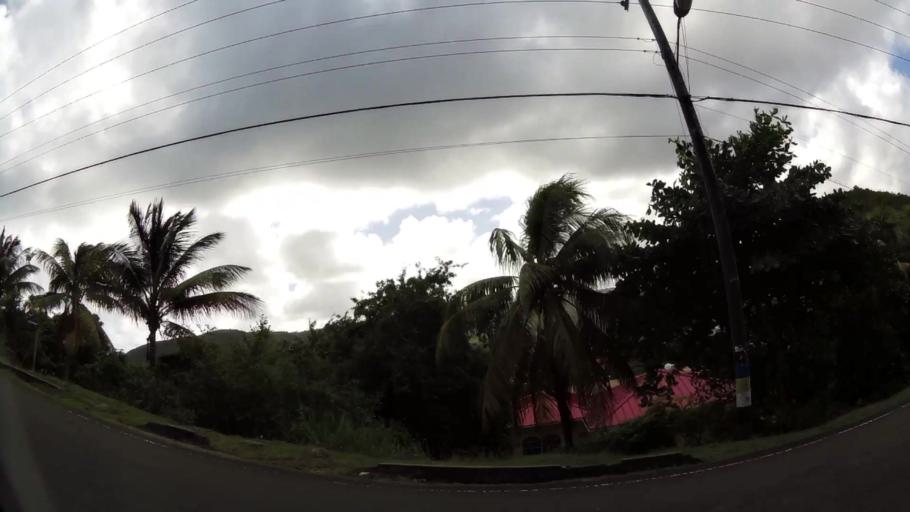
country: LC
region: Dennery Quarter
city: Dennery
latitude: 13.9156
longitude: -60.8938
